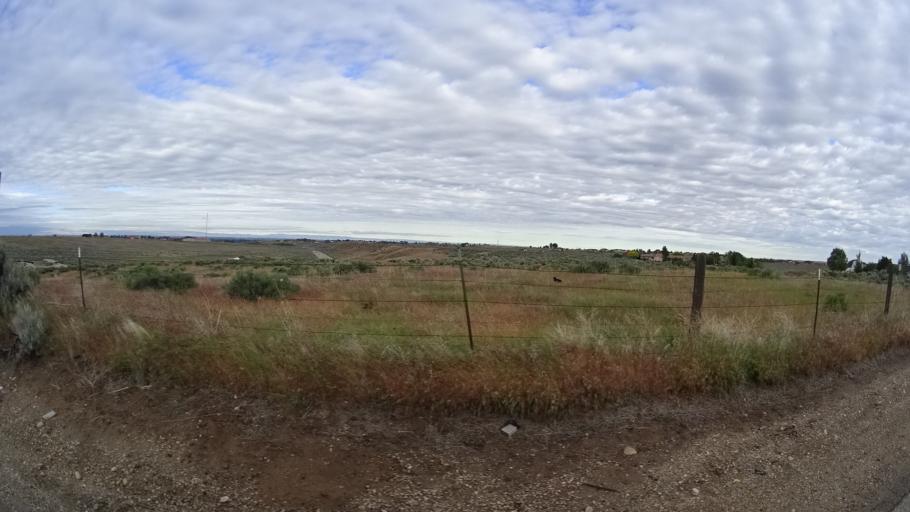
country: US
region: Idaho
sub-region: Ada County
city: Star
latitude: 43.7311
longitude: -116.5127
